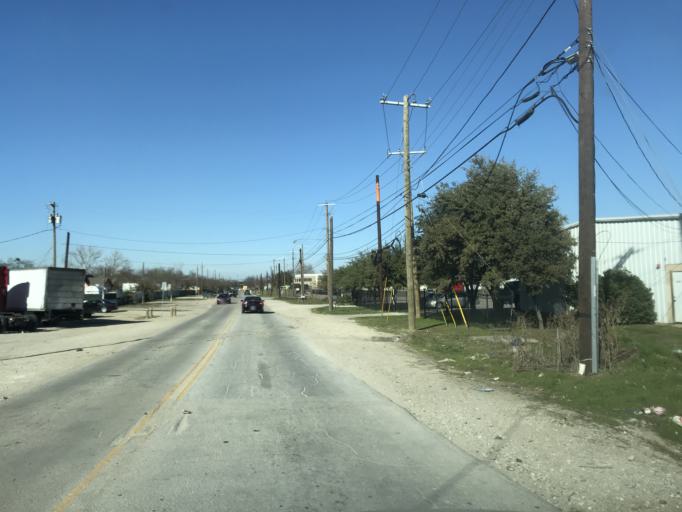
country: US
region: Texas
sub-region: Dallas County
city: Cockrell Hill
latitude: 32.7716
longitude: -96.9035
